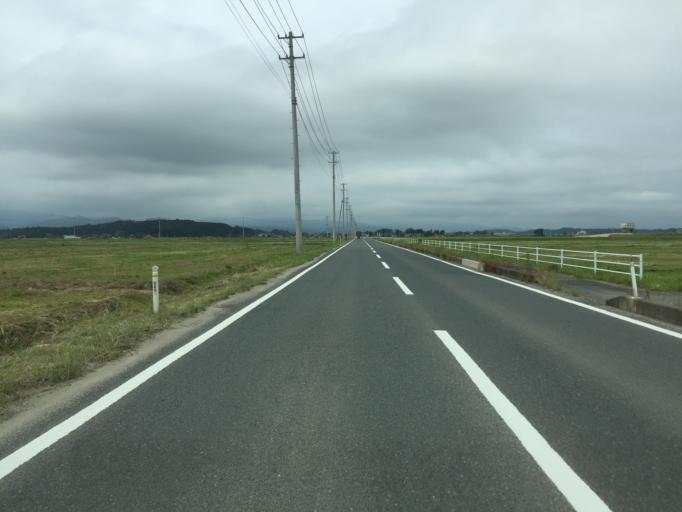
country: JP
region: Fukushima
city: Namie
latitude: 37.6828
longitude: 140.9956
